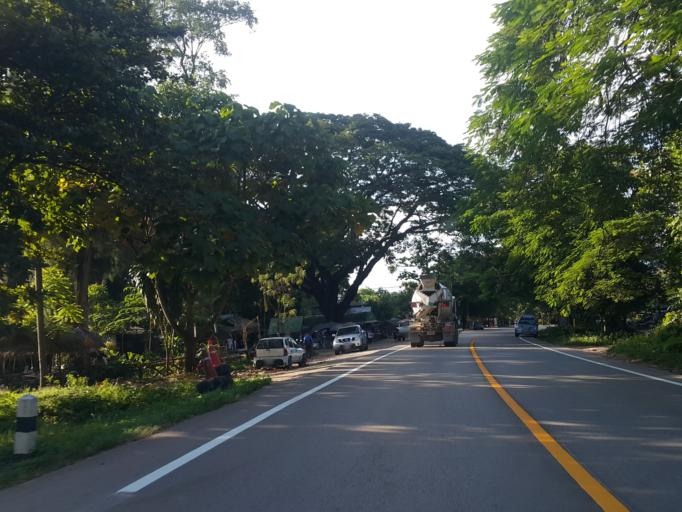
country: TH
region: Chiang Mai
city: Mae Taeng
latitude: 19.0962
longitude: 99.0820
